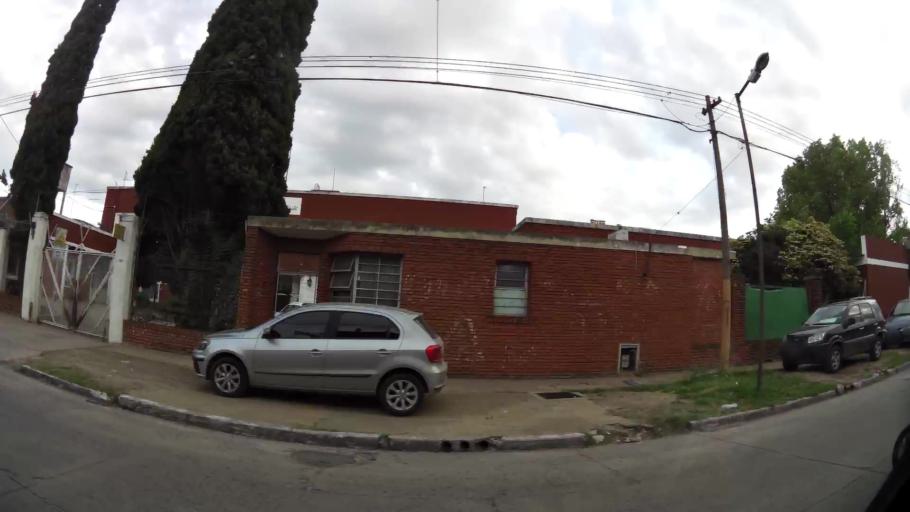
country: AR
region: Buenos Aires
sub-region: Partido de Quilmes
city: Quilmes
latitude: -34.7287
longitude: -58.2424
